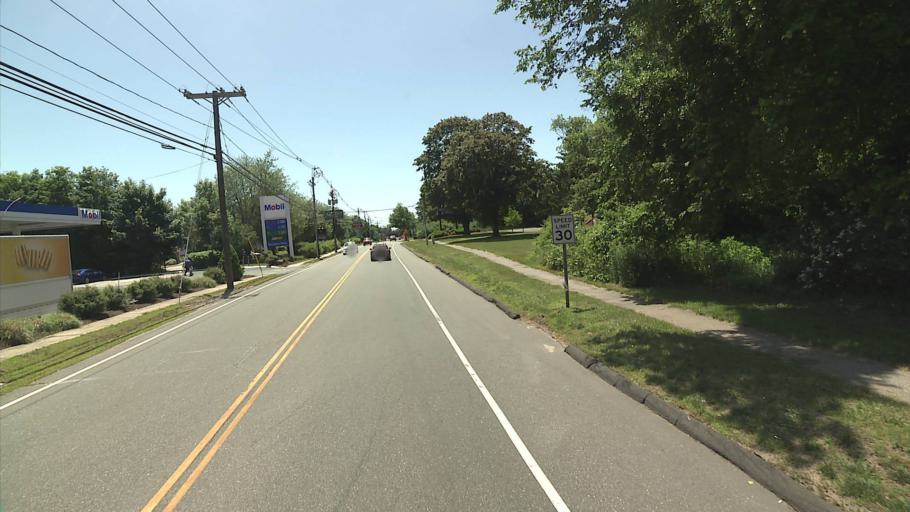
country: US
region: Connecticut
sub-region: New London County
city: Old Mystic
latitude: 41.3795
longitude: -71.9564
